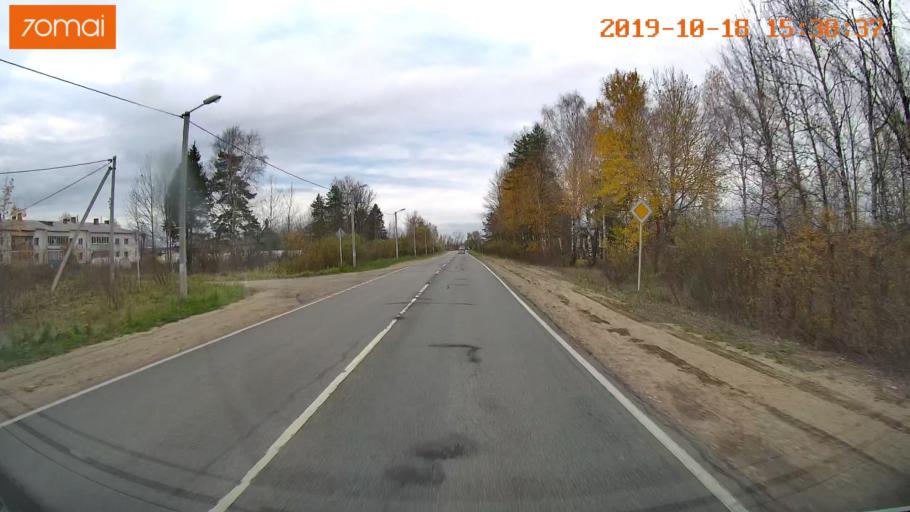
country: RU
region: Vladimir
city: Golovino
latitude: 55.9135
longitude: 40.6074
